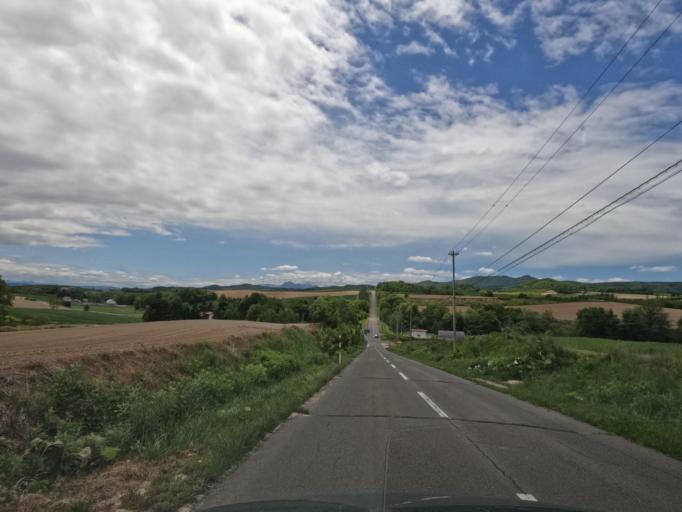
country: JP
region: Hokkaido
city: Shimo-furano
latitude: 43.5157
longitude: 142.4263
